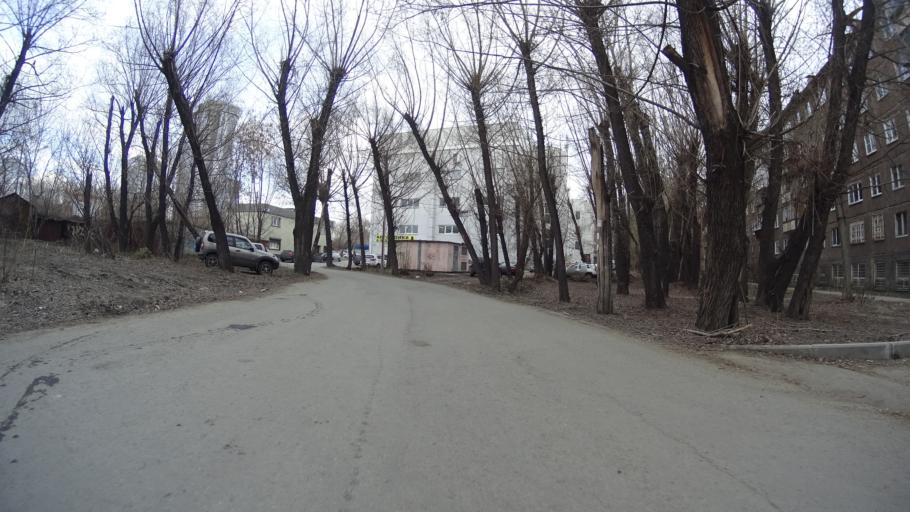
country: RU
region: Chelyabinsk
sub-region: Gorod Chelyabinsk
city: Chelyabinsk
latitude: 55.1630
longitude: 61.4256
